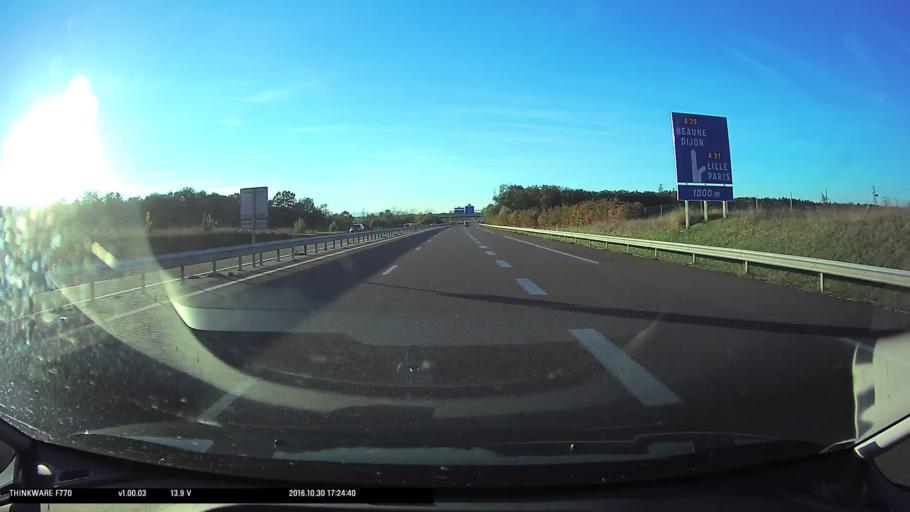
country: FR
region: Bourgogne
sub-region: Departement de la Cote-d'Or
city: Chevigny-Saint-Sauveur
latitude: 47.2700
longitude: 5.1636
